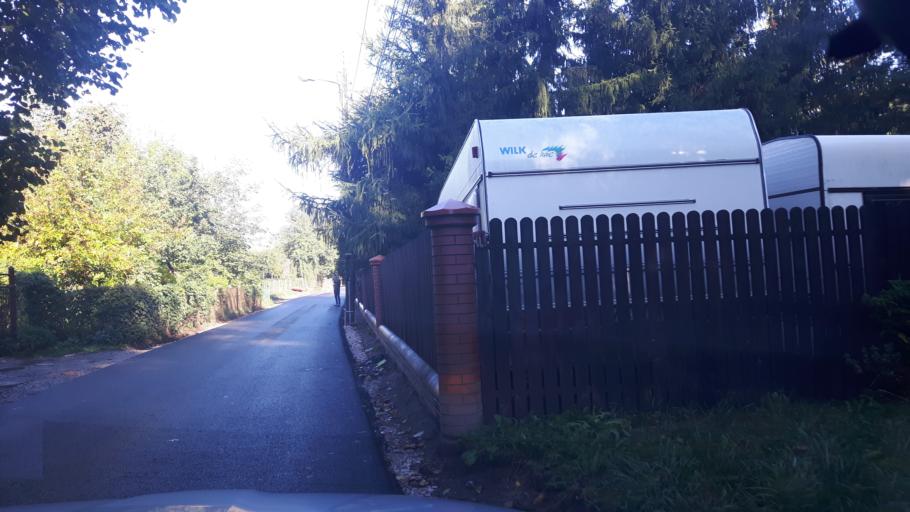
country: PL
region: Masovian Voivodeship
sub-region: Powiat legionowski
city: Stanislawow Pierwszy
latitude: 52.3584
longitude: 21.0318
